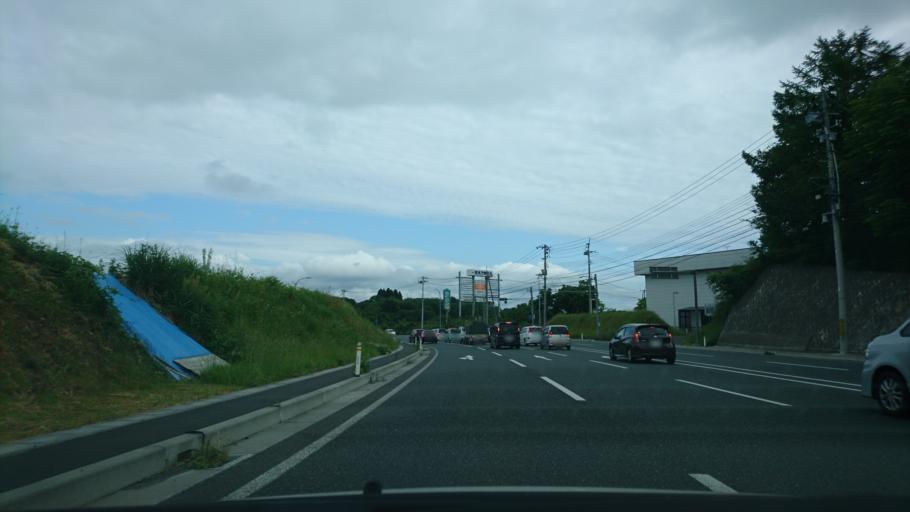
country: JP
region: Iwate
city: Ichinoseki
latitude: 38.9110
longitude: 141.1599
